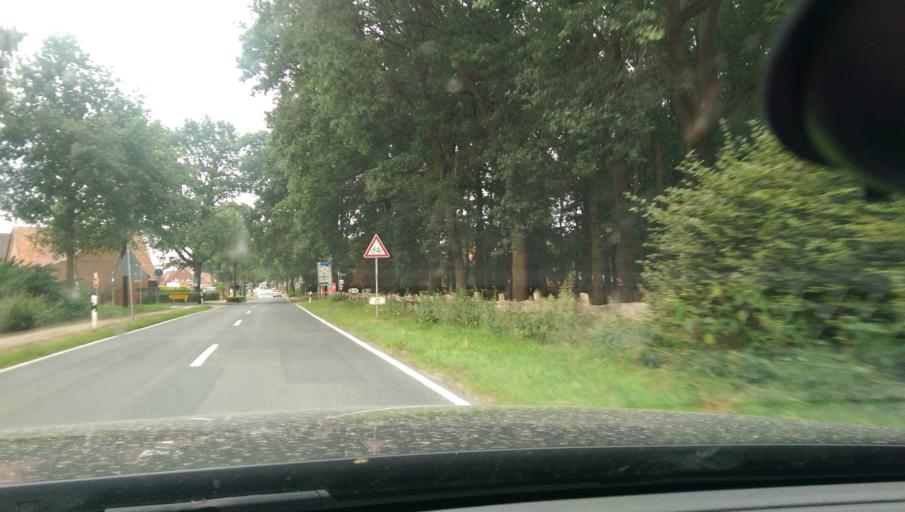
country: DE
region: Lower Saxony
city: Hagenburg
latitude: 52.4933
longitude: 9.2954
